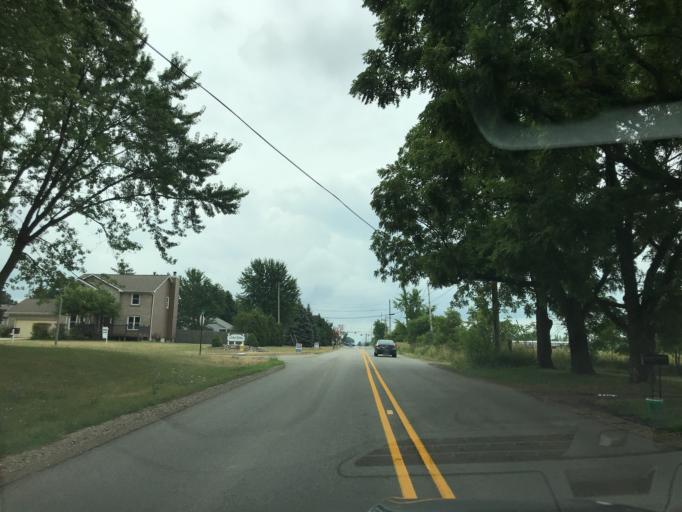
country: US
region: Michigan
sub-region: Eaton County
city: Waverly
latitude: 42.7148
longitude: -84.6621
